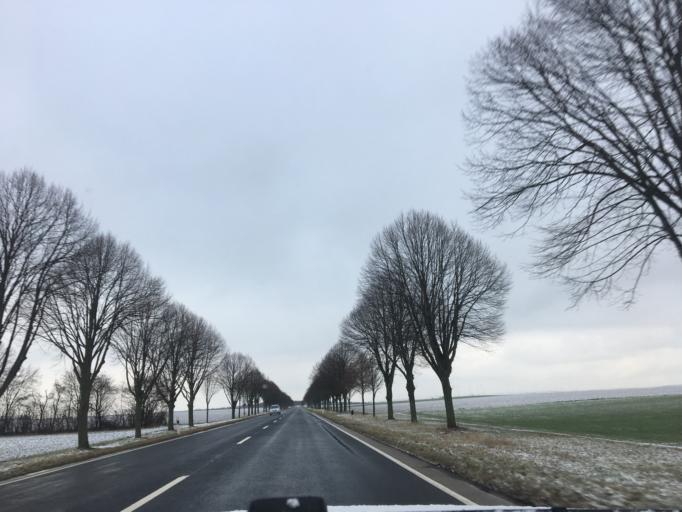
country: DE
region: Rheinland-Pfalz
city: Mauchenheim
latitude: 49.7075
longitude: 8.0541
